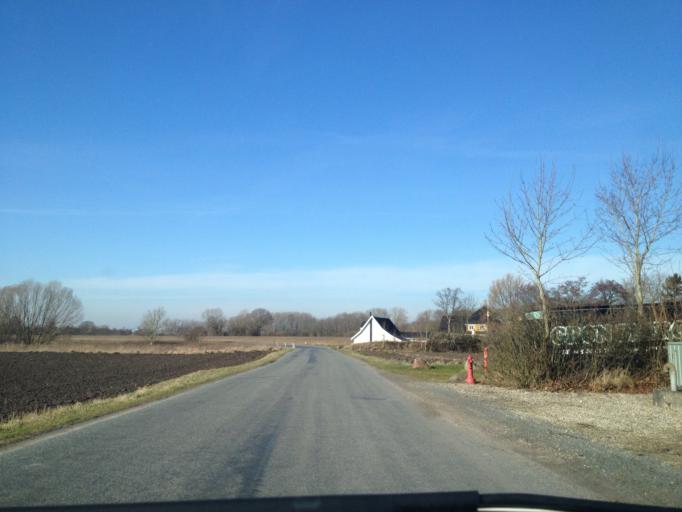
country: DK
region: South Denmark
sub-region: Nyborg Kommune
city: Ullerslev
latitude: 55.3830
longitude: 10.7203
